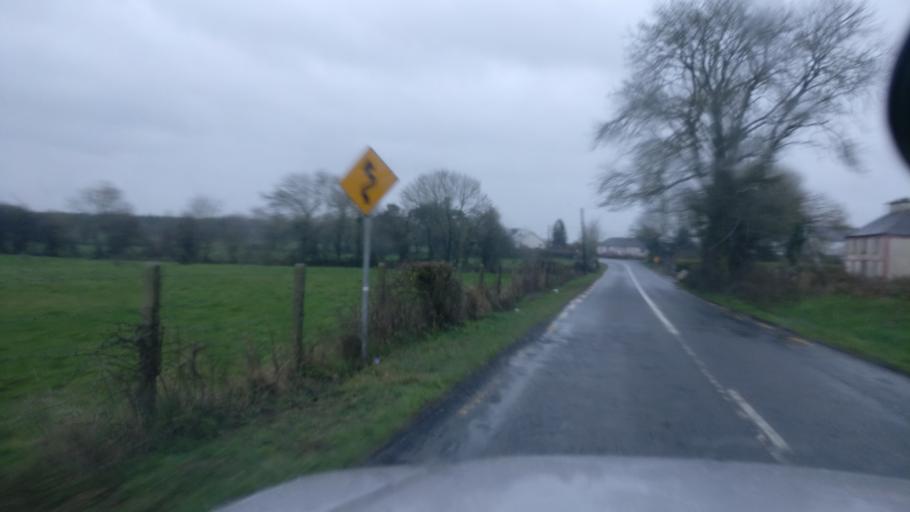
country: IE
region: Connaught
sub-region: County Galway
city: Ballinasloe
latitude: 53.2471
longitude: -8.1757
